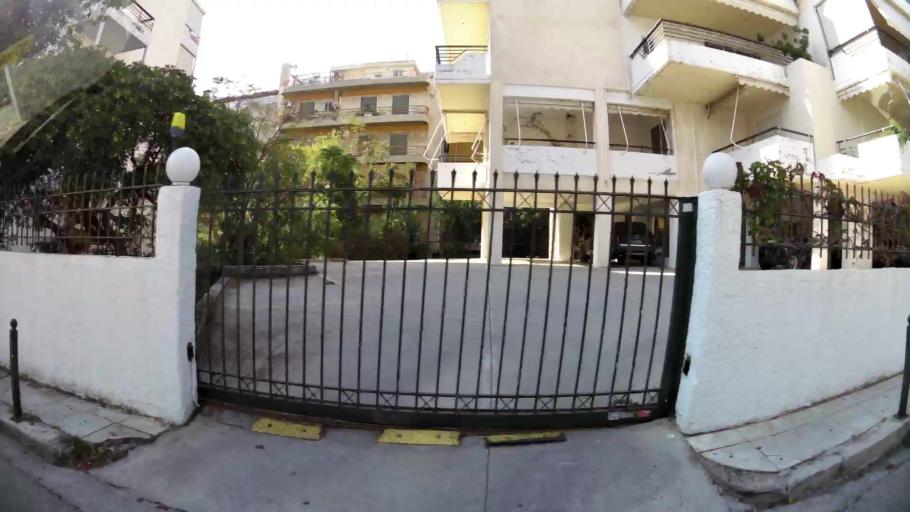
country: GR
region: Attica
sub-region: Nomarchia Athinas
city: Ilioupoli
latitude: 37.9458
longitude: 23.7702
